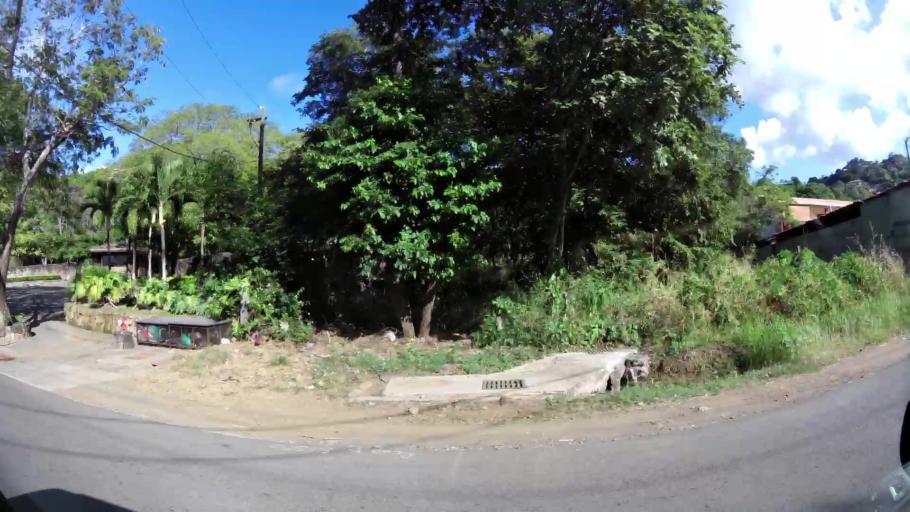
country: CR
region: Guanacaste
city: Sardinal
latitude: 10.5723
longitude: -85.6737
